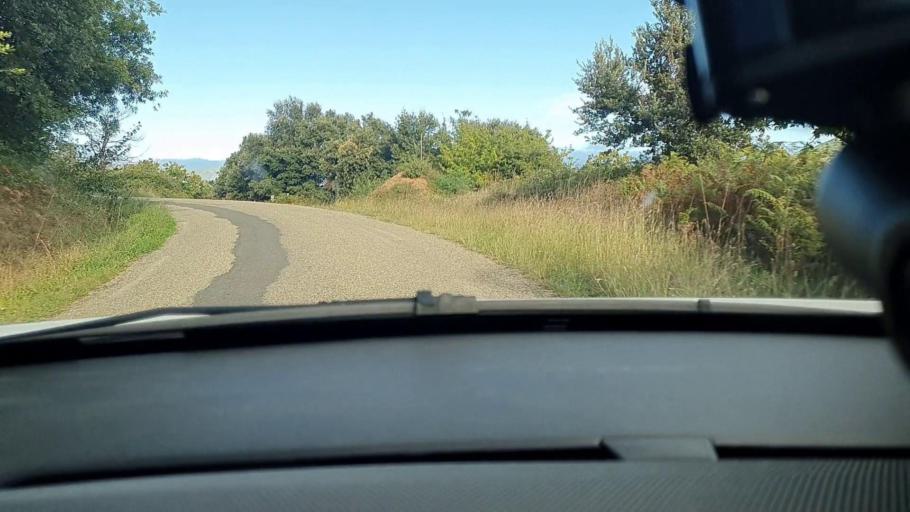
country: FR
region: Languedoc-Roussillon
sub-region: Departement du Gard
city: Besseges
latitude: 44.3251
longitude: 4.0348
